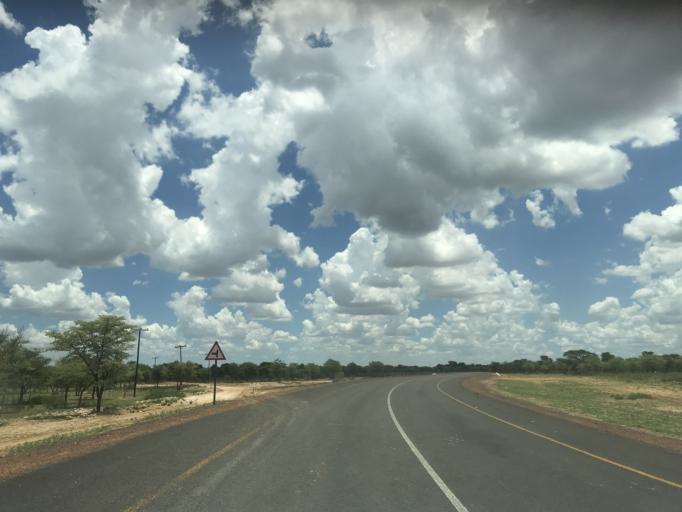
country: BW
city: Mabuli
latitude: -25.8043
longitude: 24.8142
